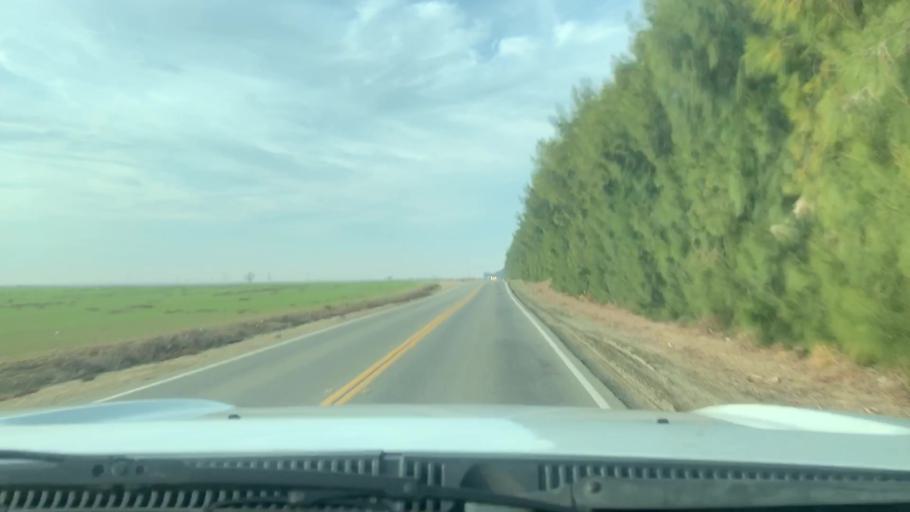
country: US
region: California
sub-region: Kern County
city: Lost Hills
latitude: 35.5159
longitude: -119.7519
